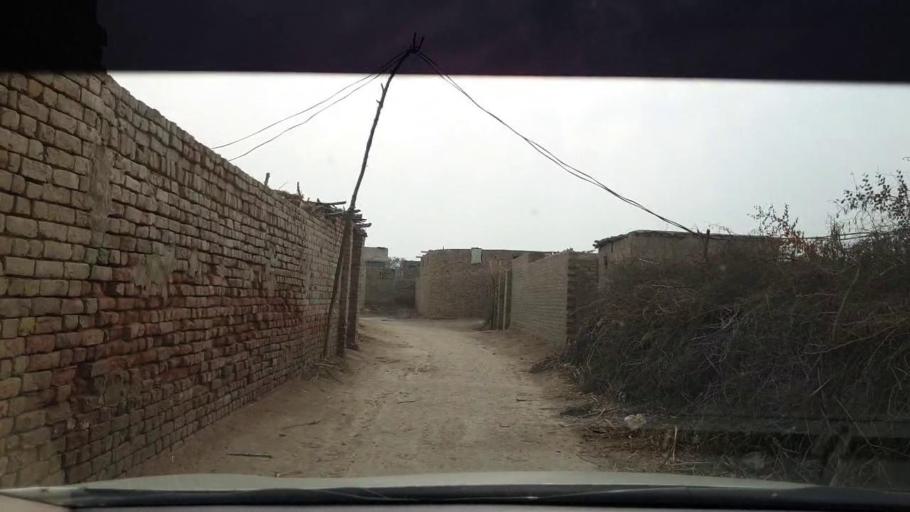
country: PK
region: Sindh
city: Berani
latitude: 25.8667
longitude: 68.7864
